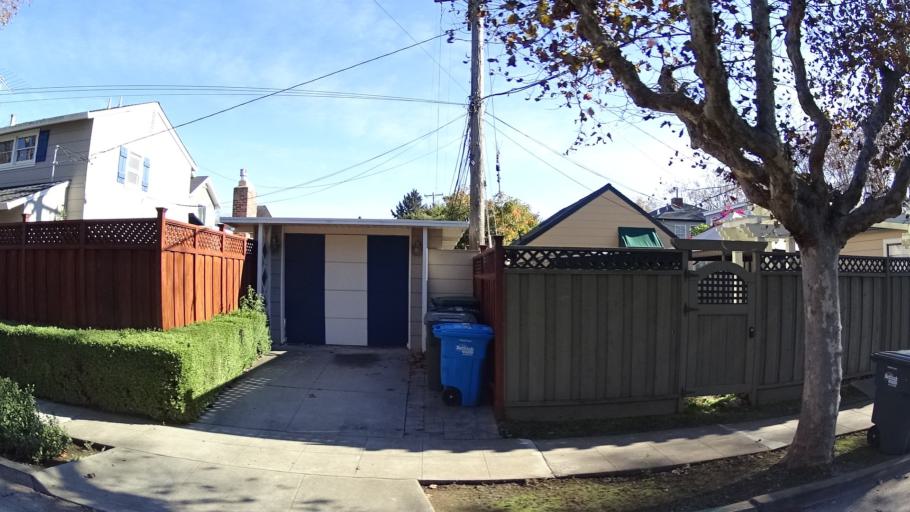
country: US
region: California
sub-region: San Mateo County
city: Burlingame
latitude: 37.5853
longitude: -122.3468
